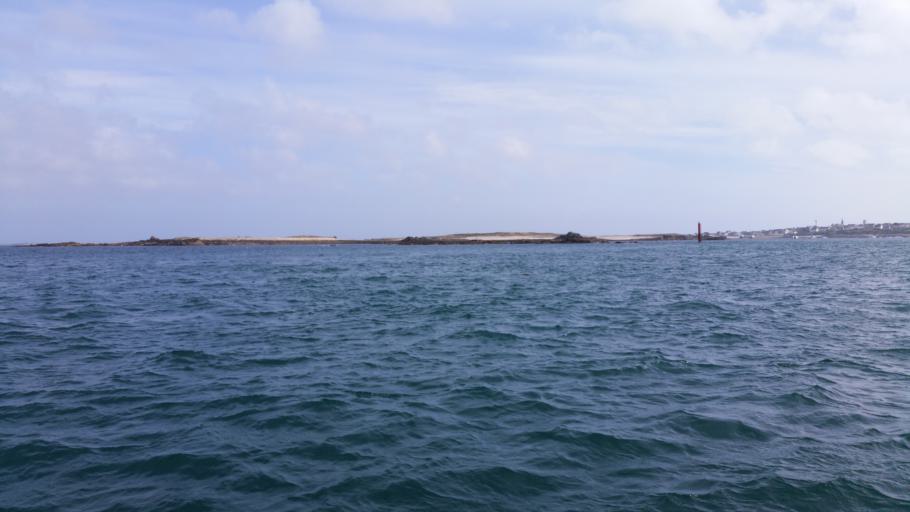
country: FR
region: Brittany
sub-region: Departement du Finistere
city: Le Conquet
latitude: 48.4121
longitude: -4.9498
